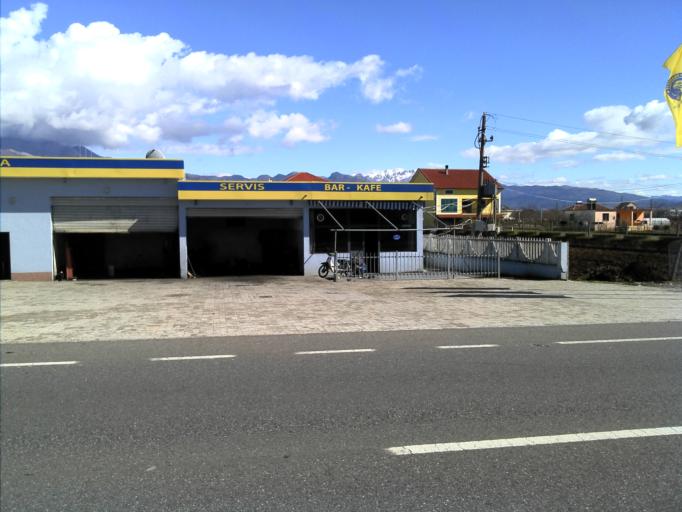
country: AL
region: Shkoder
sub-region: Rrethi i Malesia e Madhe
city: Grude-Fushe
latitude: 42.1297
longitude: 19.4910
